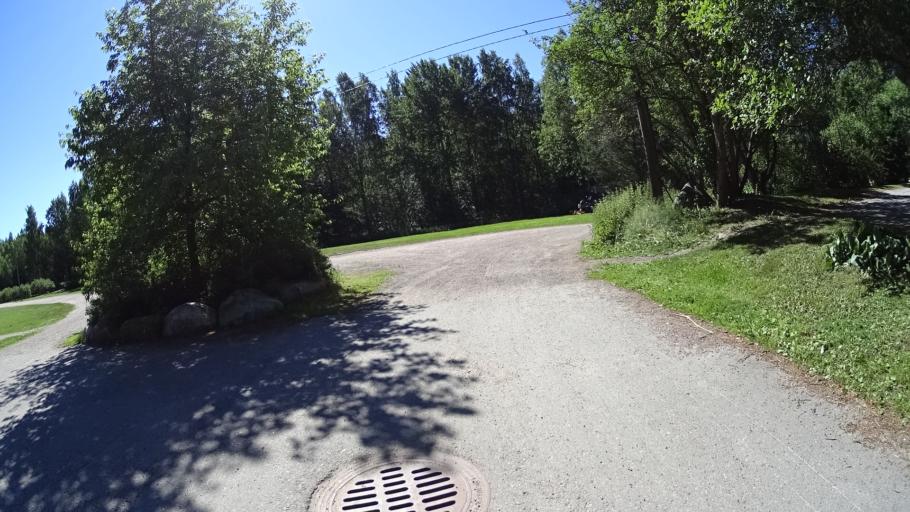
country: FI
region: Uusimaa
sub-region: Helsinki
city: Espoo
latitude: 60.1473
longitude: 24.6927
